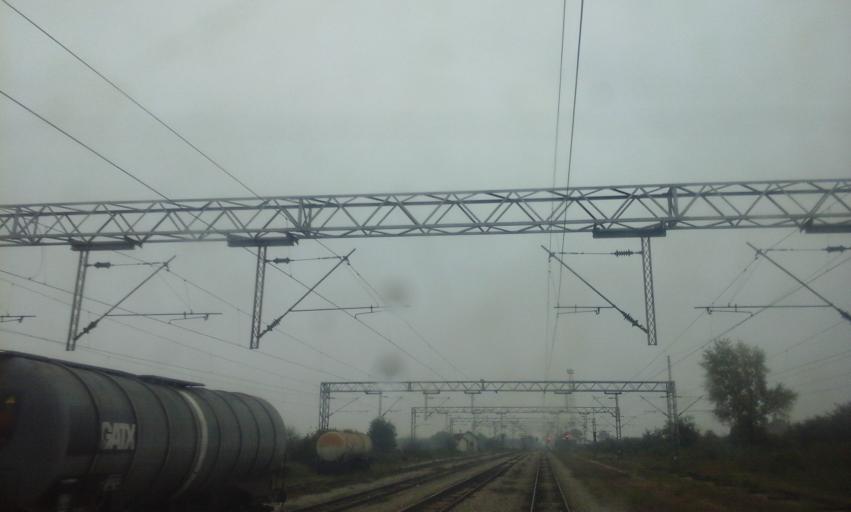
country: RS
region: Central Serbia
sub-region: Pomoravski Okrug
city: Paracin
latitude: 43.8650
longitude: 21.3987
